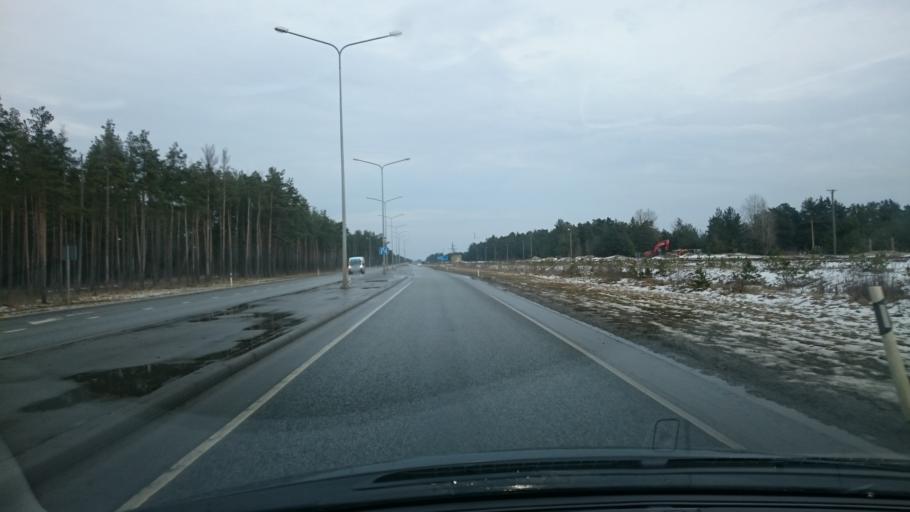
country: EE
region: Harju
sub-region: Saku vald
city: Saku
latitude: 59.3410
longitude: 24.7025
